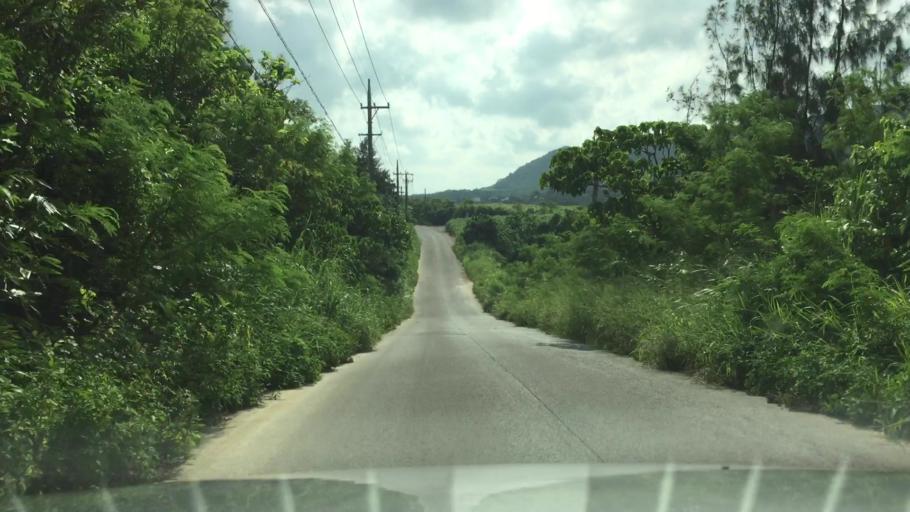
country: JP
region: Okinawa
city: Ishigaki
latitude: 24.4001
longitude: 124.2069
